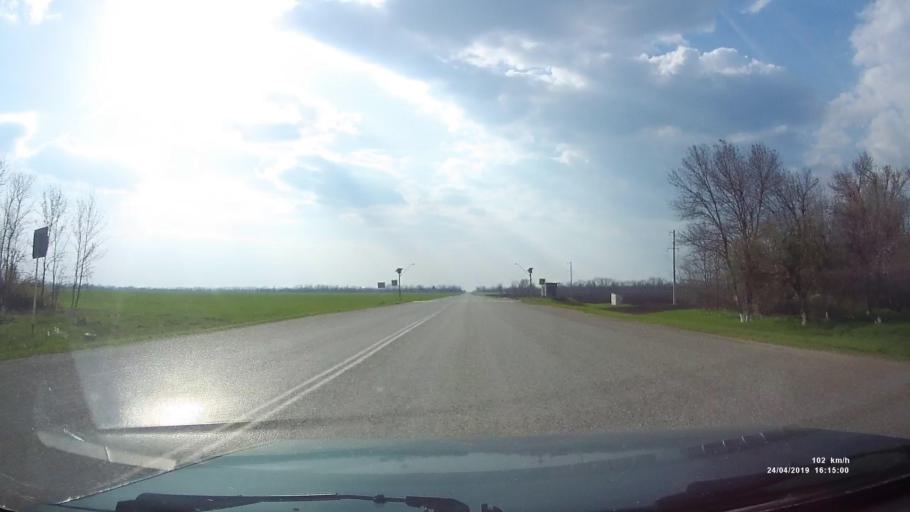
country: RU
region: Rostov
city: Sovetskoye
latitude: 46.7551
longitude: 42.1904
